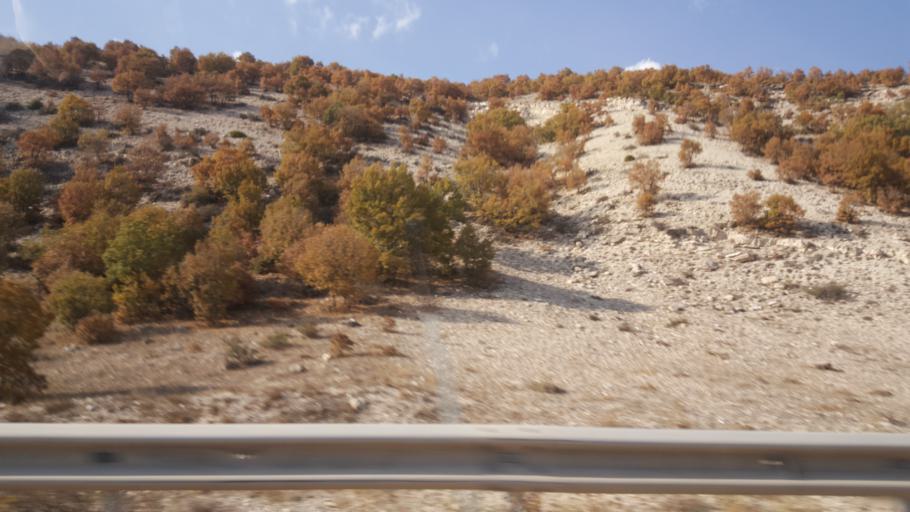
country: TR
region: Eskisehir
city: Kirka
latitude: 39.3432
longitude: 30.5797
